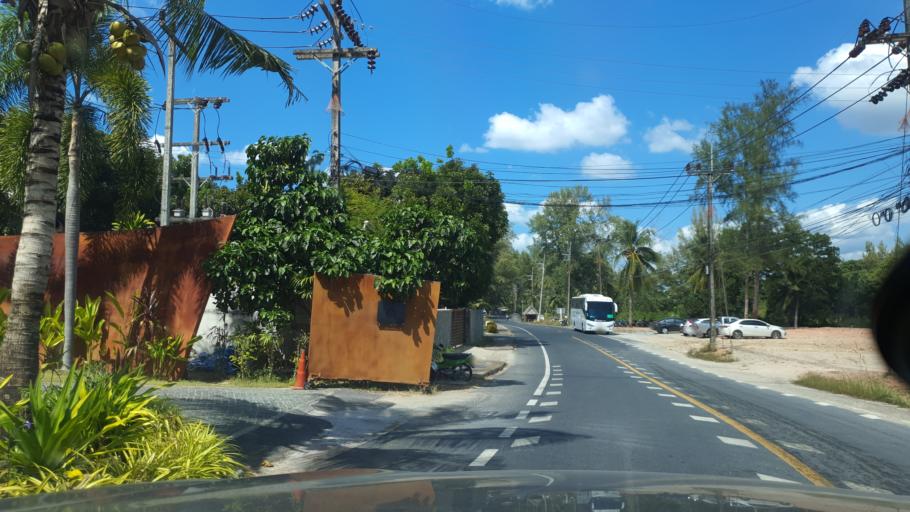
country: TH
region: Phangnga
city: Thai Mueang
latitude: 8.2869
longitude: 98.2750
